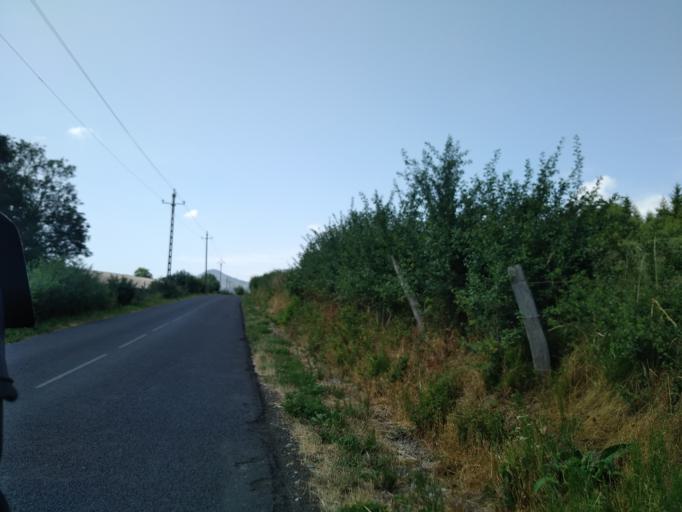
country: FR
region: Auvergne
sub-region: Departement du Cantal
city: Riom-es-Montagnes
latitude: 45.1740
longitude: 2.7166
